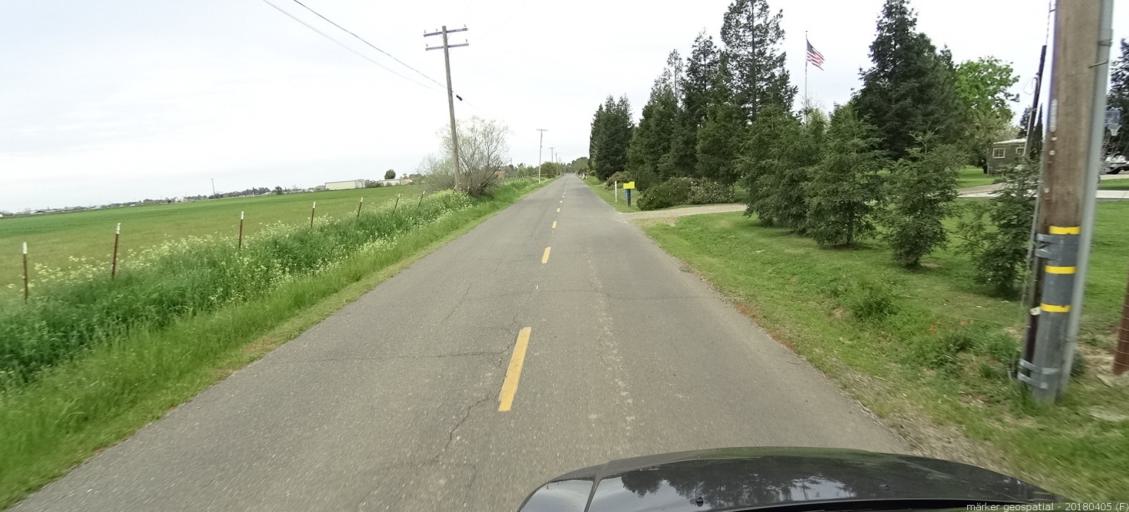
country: US
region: California
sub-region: Sacramento County
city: Herald
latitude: 38.2773
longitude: -121.2373
